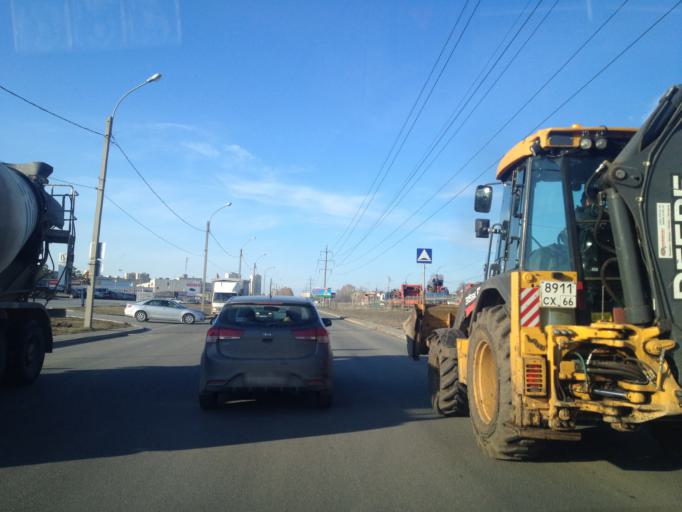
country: RU
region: Sverdlovsk
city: Sovkhoznyy
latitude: 56.7590
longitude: 60.5883
